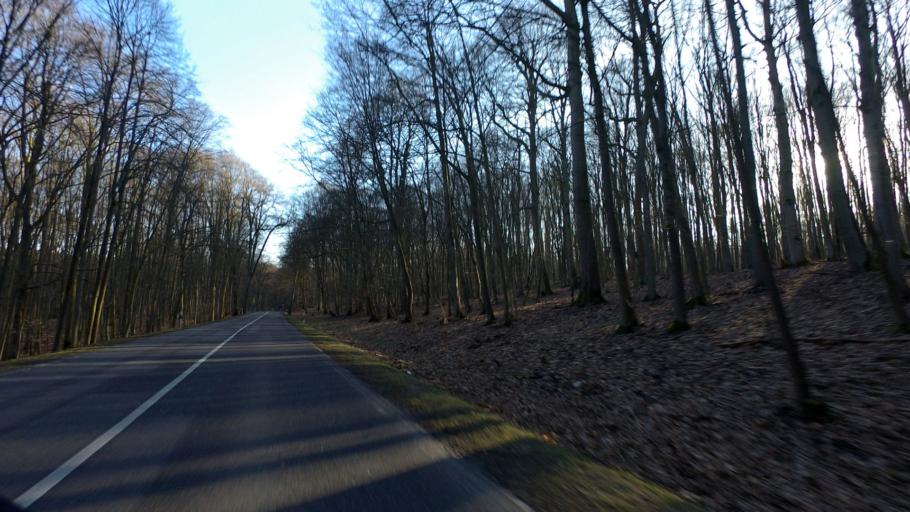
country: DE
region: Brandenburg
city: Althuttendorf
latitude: 52.9448
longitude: 13.7838
